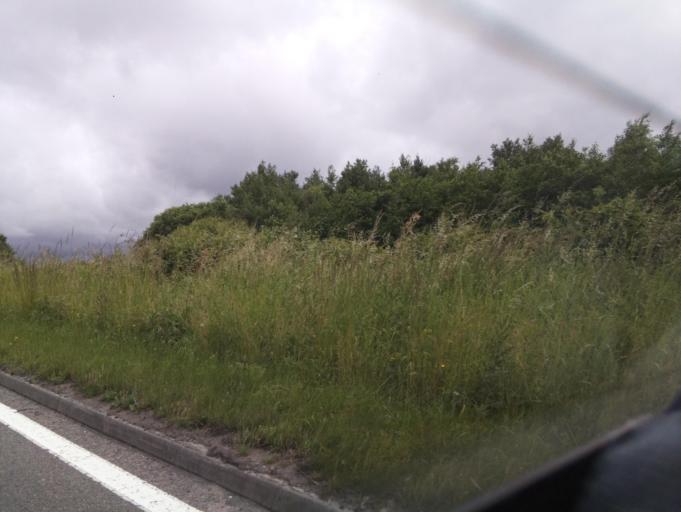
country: GB
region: England
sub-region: Leicestershire
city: Ashby de la Zouch
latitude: 52.7573
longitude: -1.4547
